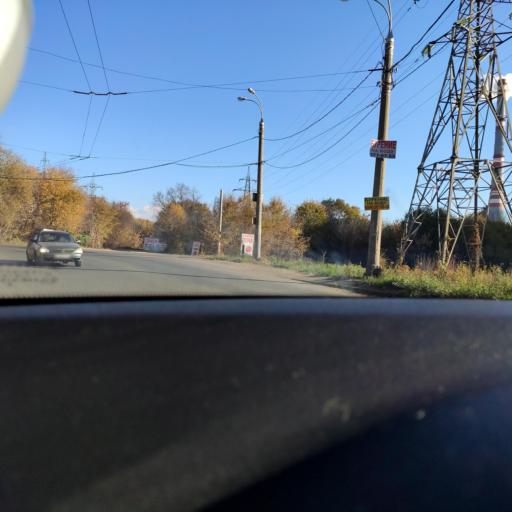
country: RU
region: Samara
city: Petra-Dubrava
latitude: 53.2508
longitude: 50.2675
